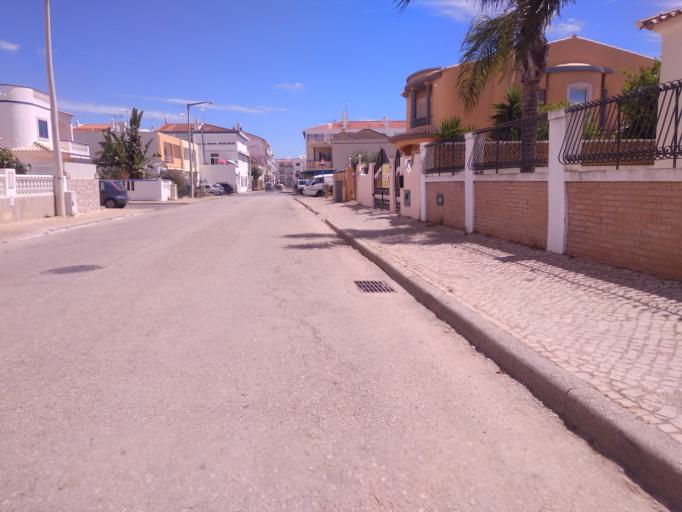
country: PT
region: Faro
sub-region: Sao Bras de Alportel
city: Sao Bras de Alportel
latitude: 37.1538
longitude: -7.8829
